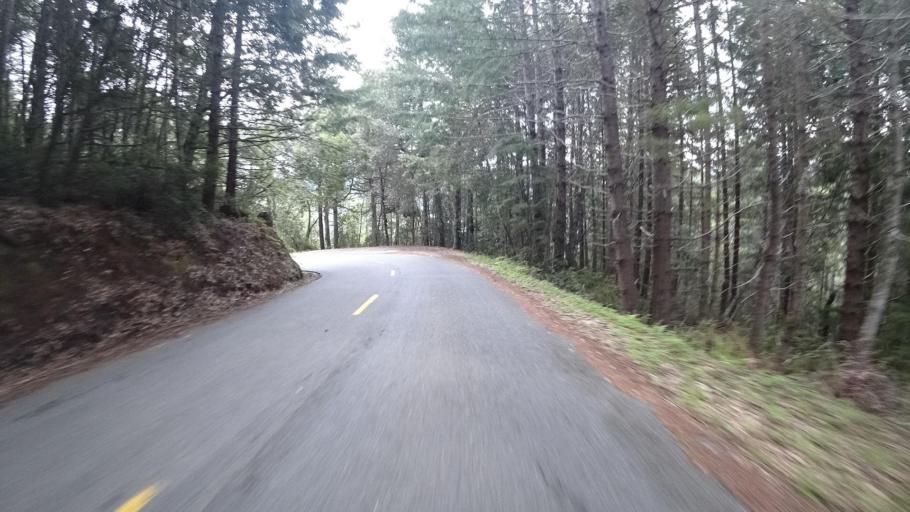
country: US
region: California
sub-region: Humboldt County
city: Blue Lake
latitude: 40.9378
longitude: -123.8439
